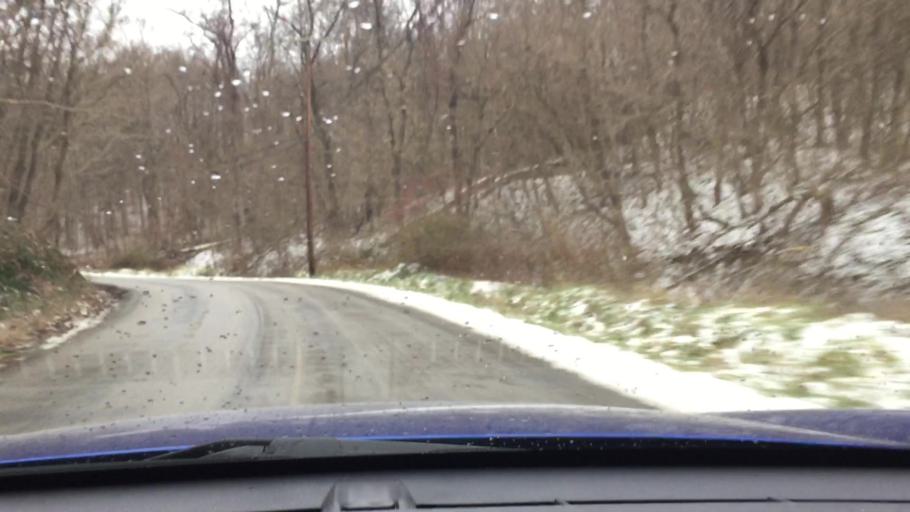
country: US
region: Pennsylvania
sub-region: Westmoreland County
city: Fellsburg
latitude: 40.1689
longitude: -79.8341
